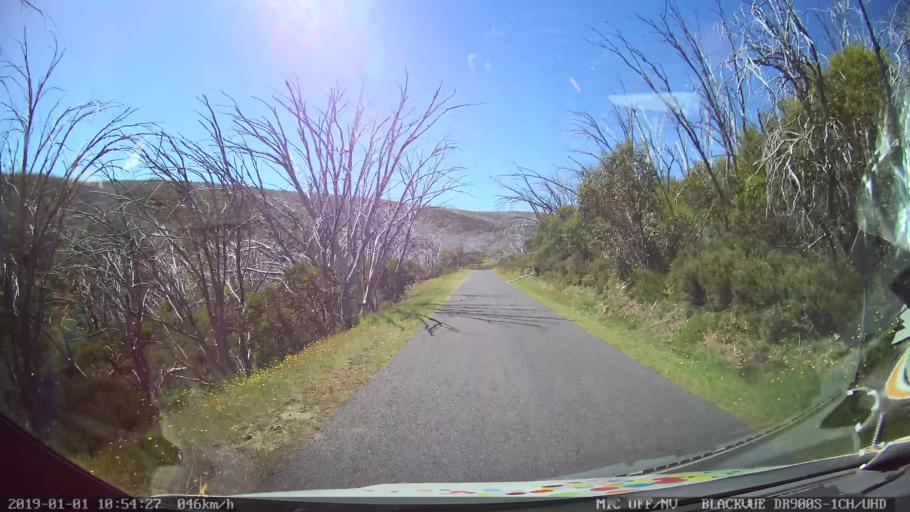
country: AU
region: New South Wales
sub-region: Snowy River
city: Jindabyne
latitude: -36.0097
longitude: 148.3846
